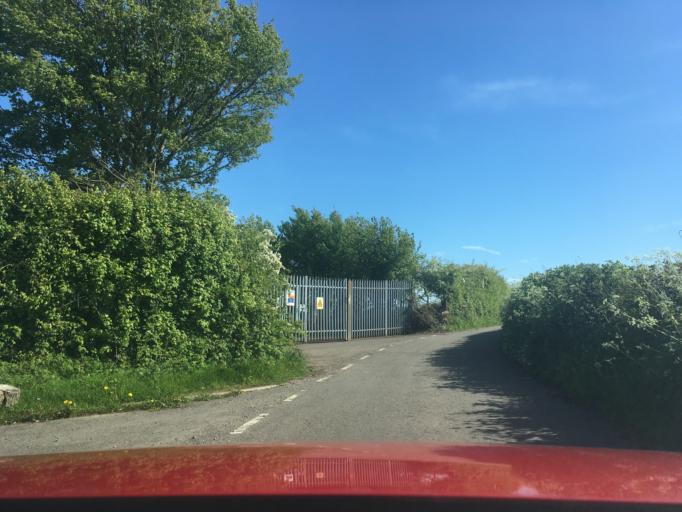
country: GB
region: Wales
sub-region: Newport
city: Marshfield
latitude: 51.5582
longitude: -3.0669
